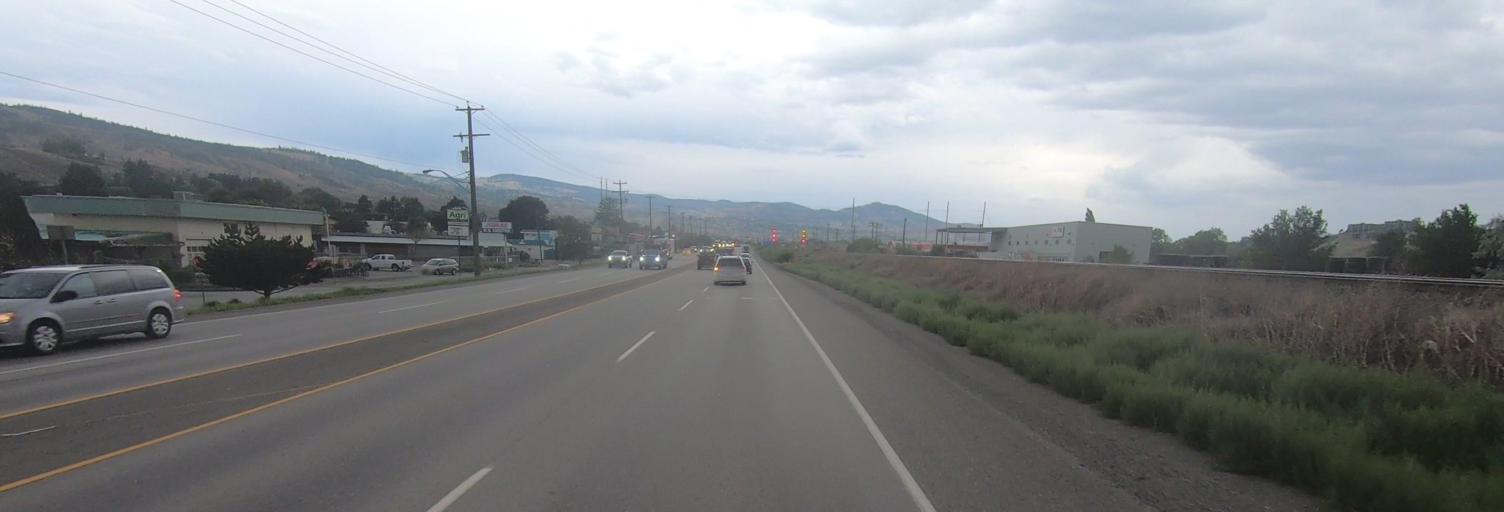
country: CA
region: British Columbia
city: Kamloops
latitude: 50.6803
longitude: -120.2749
